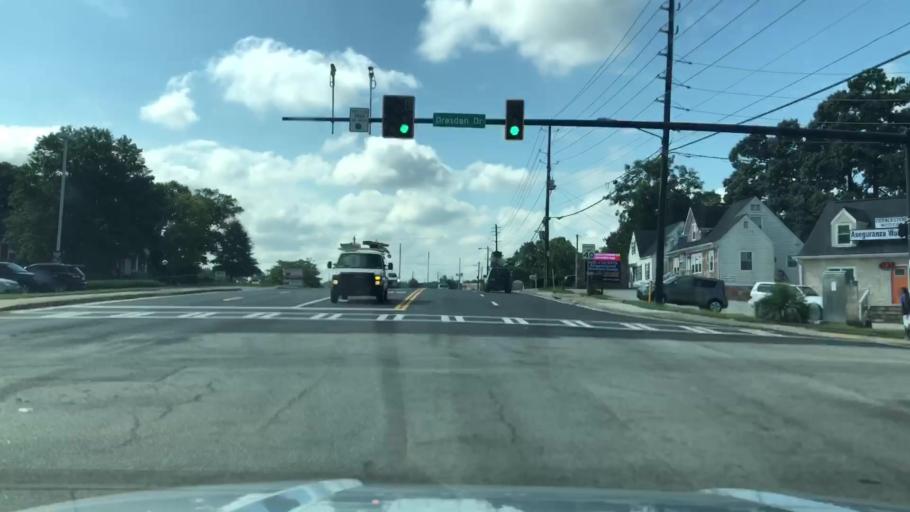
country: US
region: Georgia
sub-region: DeKalb County
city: North Atlanta
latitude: 33.8654
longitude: -84.3095
